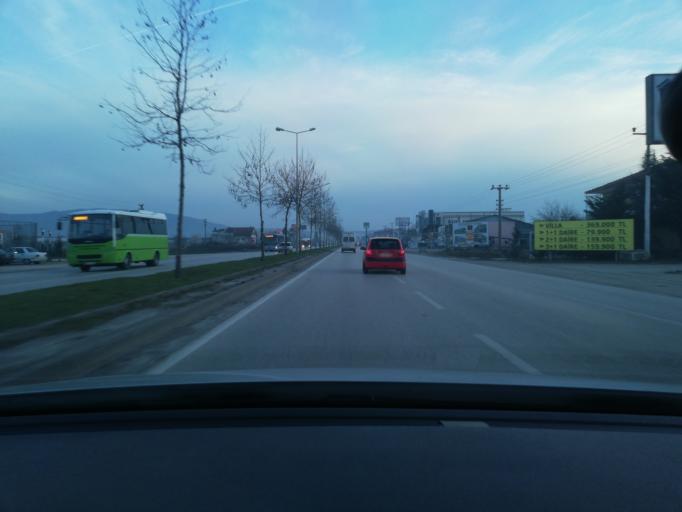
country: TR
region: Duzce
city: Duzce
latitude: 40.8595
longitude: 31.1671
